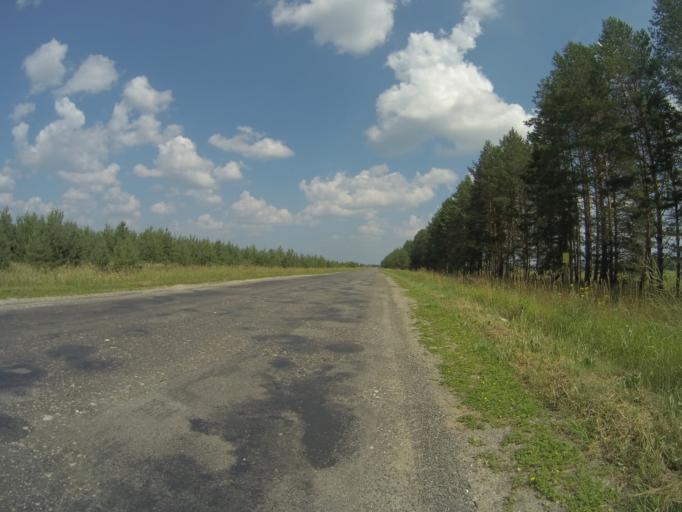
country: RU
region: Vladimir
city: Anopino
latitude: 55.6549
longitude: 40.8412
